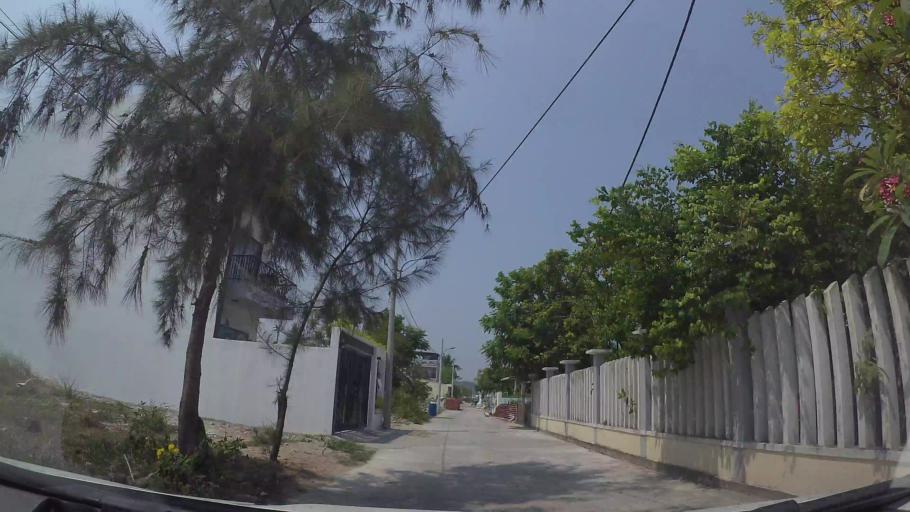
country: VN
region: Da Nang
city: Ngu Hanh Son
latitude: 15.9930
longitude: 108.2639
